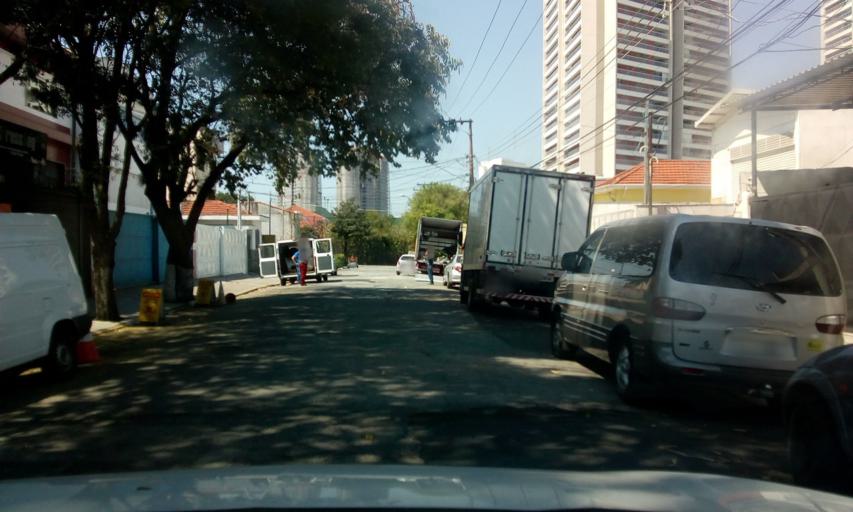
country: BR
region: Sao Paulo
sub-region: Osasco
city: Osasco
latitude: -23.5158
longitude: -46.7191
